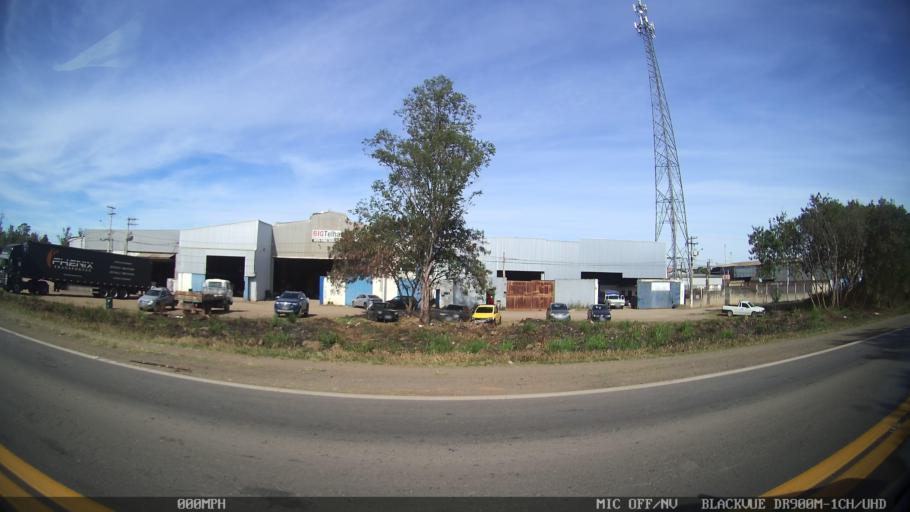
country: BR
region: Sao Paulo
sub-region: Rio Das Pedras
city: Rio das Pedras
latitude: -22.7956
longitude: -47.6135
